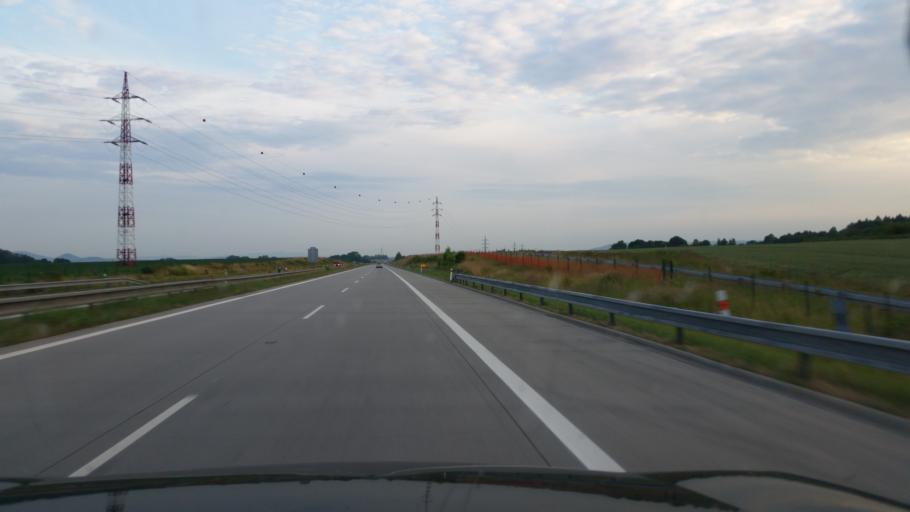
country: CZ
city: Bilovec
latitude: 49.7213
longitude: 18.0092
